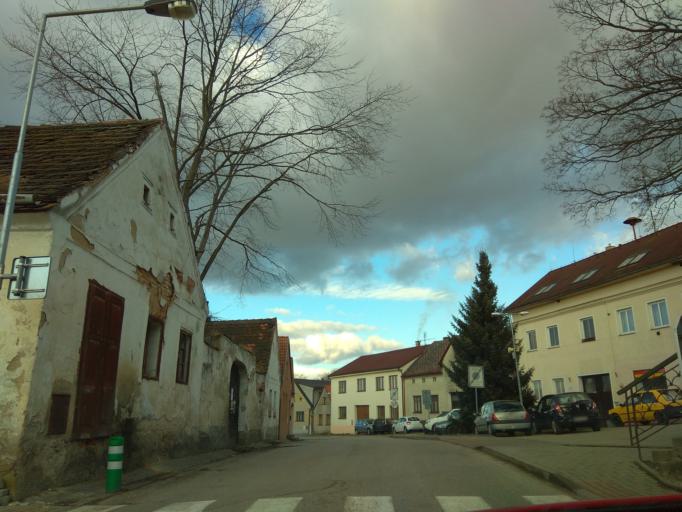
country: CZ
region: Jihocesky
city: Hrdejovice
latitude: 49.0372
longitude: 14.4758
